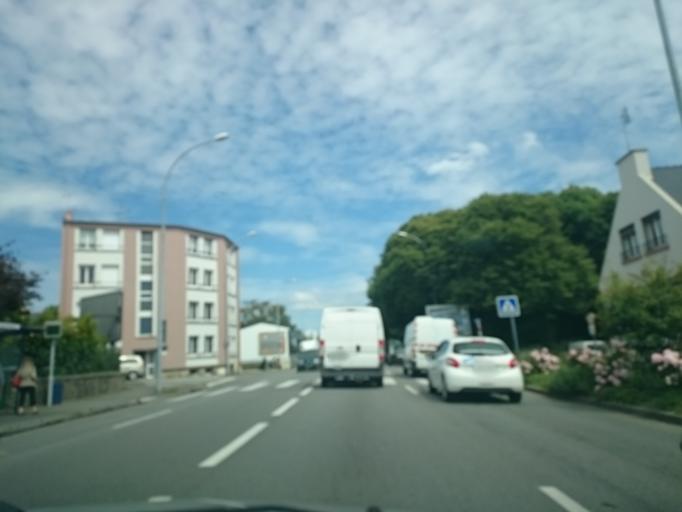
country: FR
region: Brittany
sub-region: Departement du Finistere
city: Brest
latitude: 48.4131
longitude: -4.4929
